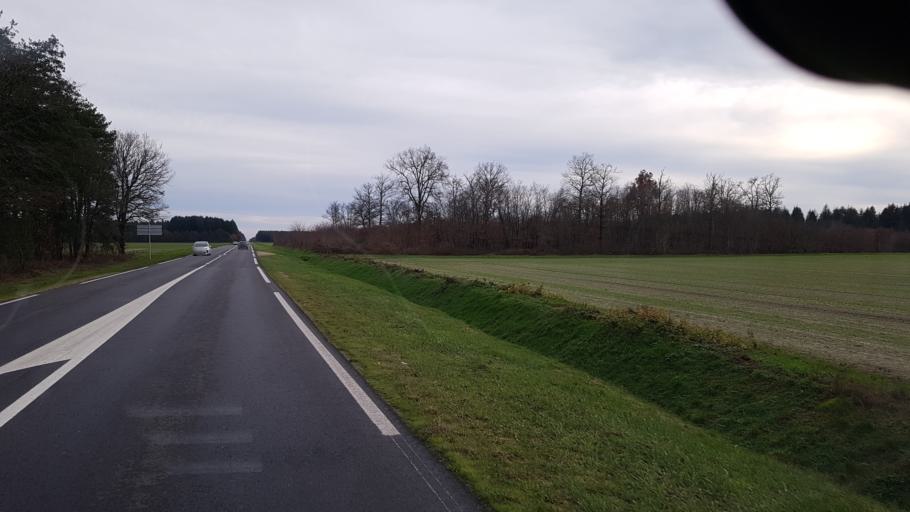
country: FR
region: Centre
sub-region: Departement du Loir-et-Cher
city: Lamotte-Beuvron
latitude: 47.6449
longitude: 1.9936
